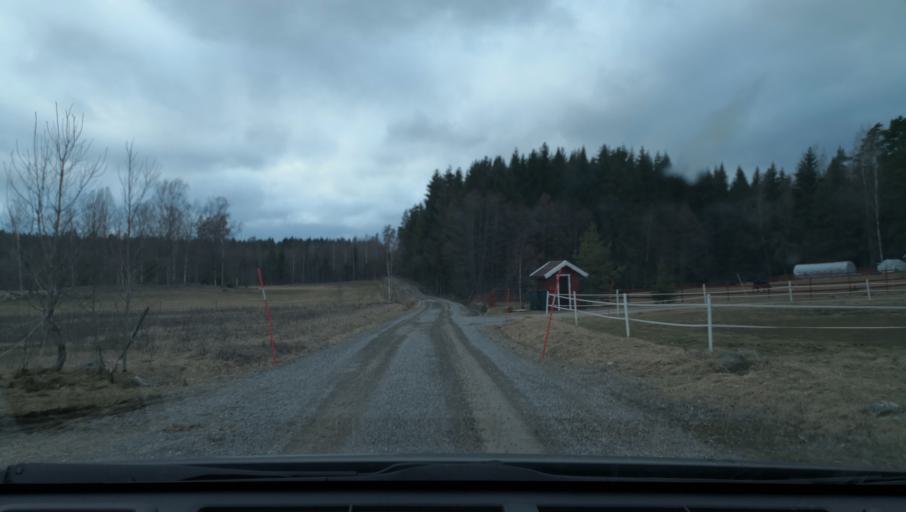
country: SE
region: Vaestmanland
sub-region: Kopings Kommun
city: Kolsva
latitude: 59.5638
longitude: 15.8307
